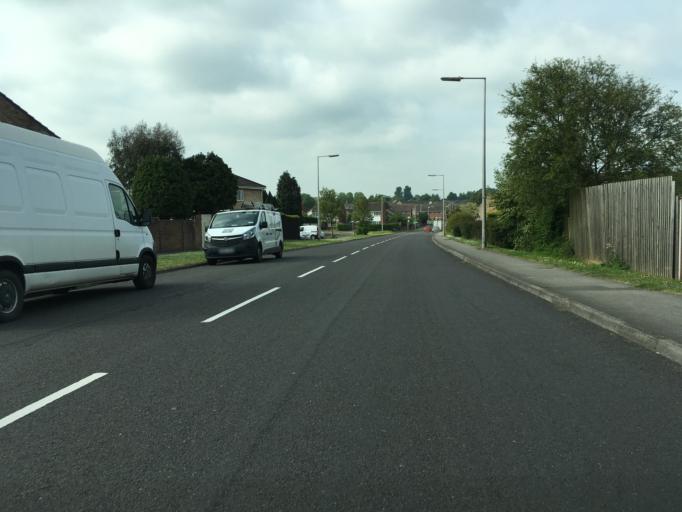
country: GB
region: England
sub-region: North Somerset
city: Nailsea
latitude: 51.4294
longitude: -2.7595
